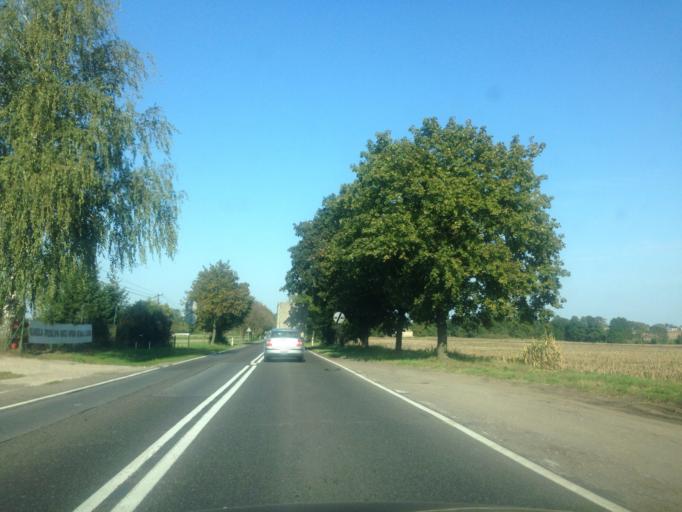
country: PL
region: Kujawsko-Pomorskie
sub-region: Powiat wabrzeski
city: Debowa Laka
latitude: 53.2096
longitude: 19.1739
